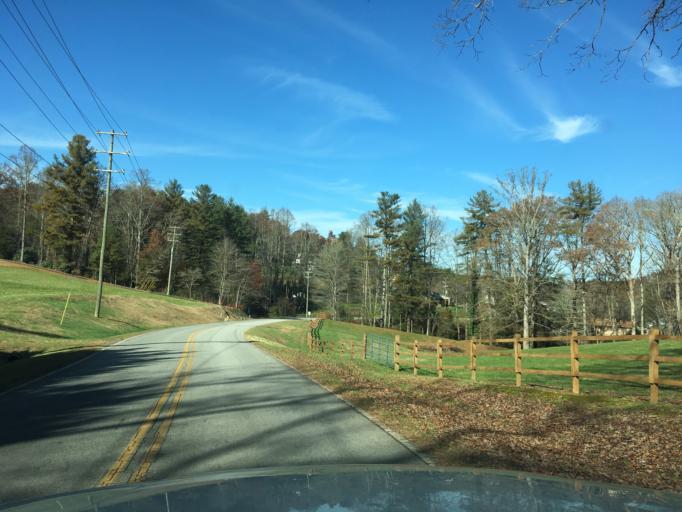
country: US
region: North Carolina
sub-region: Henderson County
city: Etowah
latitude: 35.3147
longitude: -82.6199
